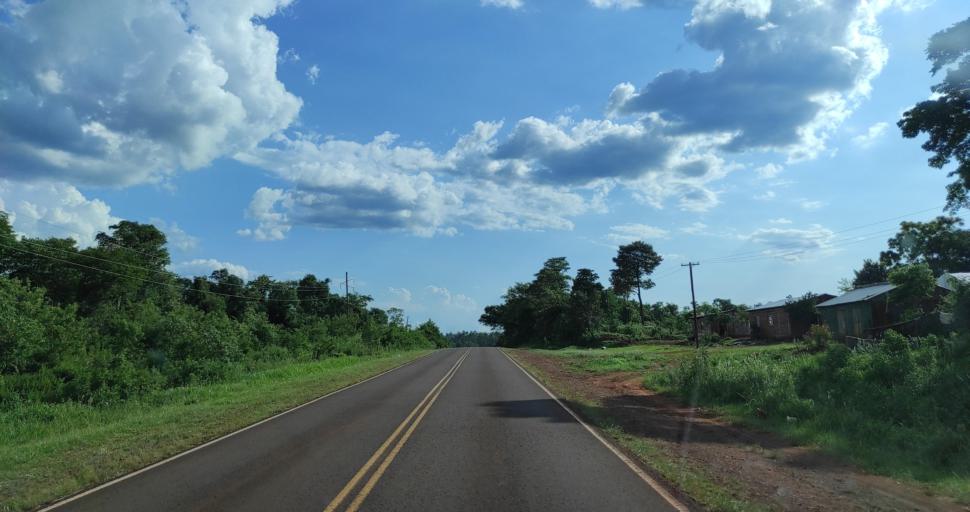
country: AR
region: Misiones
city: San Vicente
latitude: -26.3535
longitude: -54.2112
